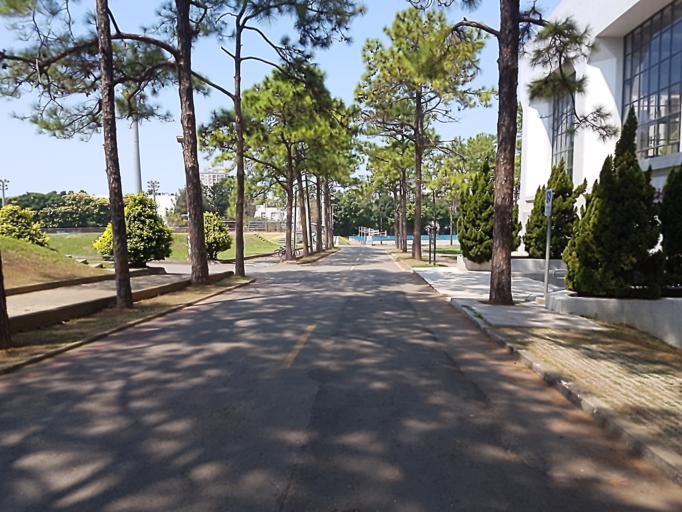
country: TW
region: Taiwan
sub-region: Hsinchu
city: Hsinchu
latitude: 24.7948
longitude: 120.9912
